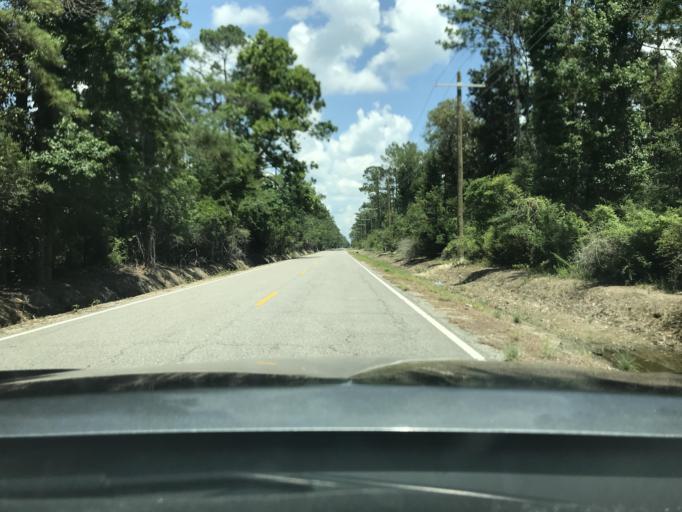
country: US
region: Louisiana
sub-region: Calcasieu Parish
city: Moss Bluff
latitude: 30.3300
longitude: -93.1587
